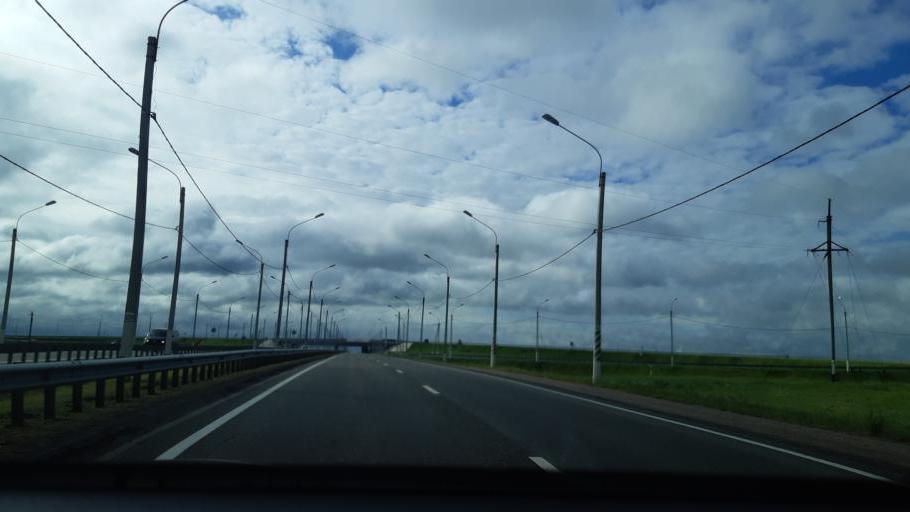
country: RU
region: Smolensk
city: Talashkino
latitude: 54.7085
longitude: 32.1148
